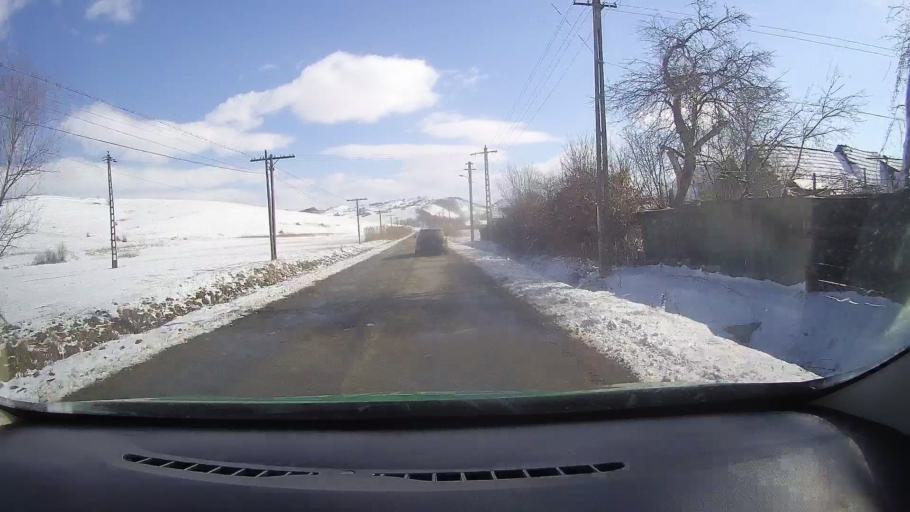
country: RO
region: Sibiu
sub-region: Comuna Altina
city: Altina
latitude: 45.9815
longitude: 24.4584
